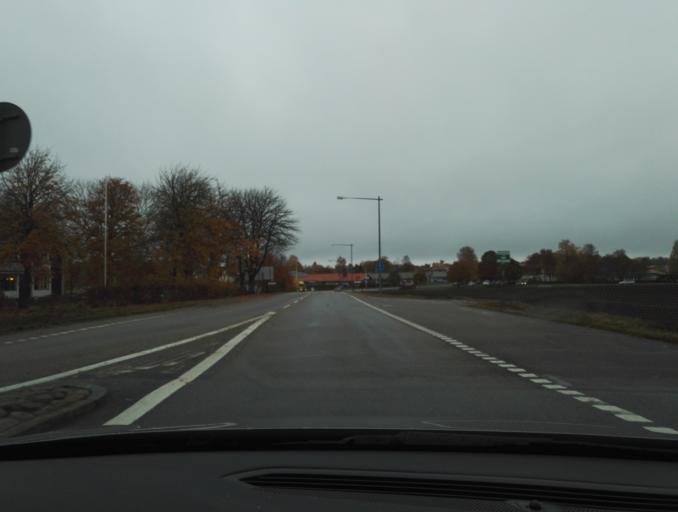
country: SE
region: Kronoberg
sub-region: Vaxjo Kommun
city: Rottne
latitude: 57.0235
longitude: 14.8843
